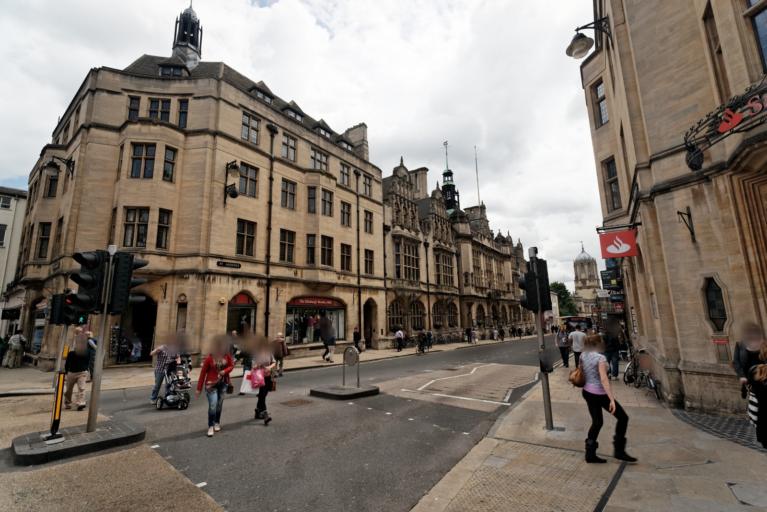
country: GB
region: England
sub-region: Oxfordshire
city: Oxford
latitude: 51.7519
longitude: -1.2578
